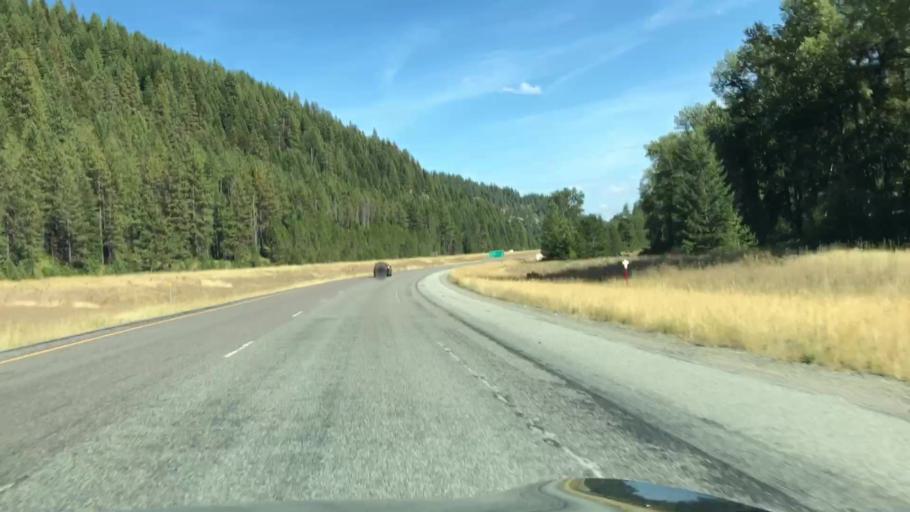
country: US
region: Montana
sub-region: Sanders County
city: Thompson Falls
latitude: 47.4074
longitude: -115.4957
